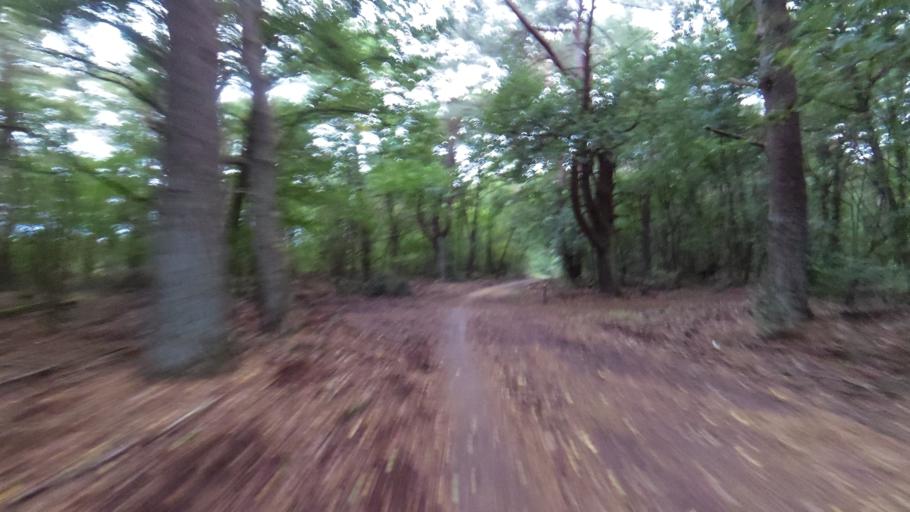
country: NL
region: Gelderland
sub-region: Gemeente Ede
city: Harskamp
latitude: 52.1807
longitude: 5.7801
